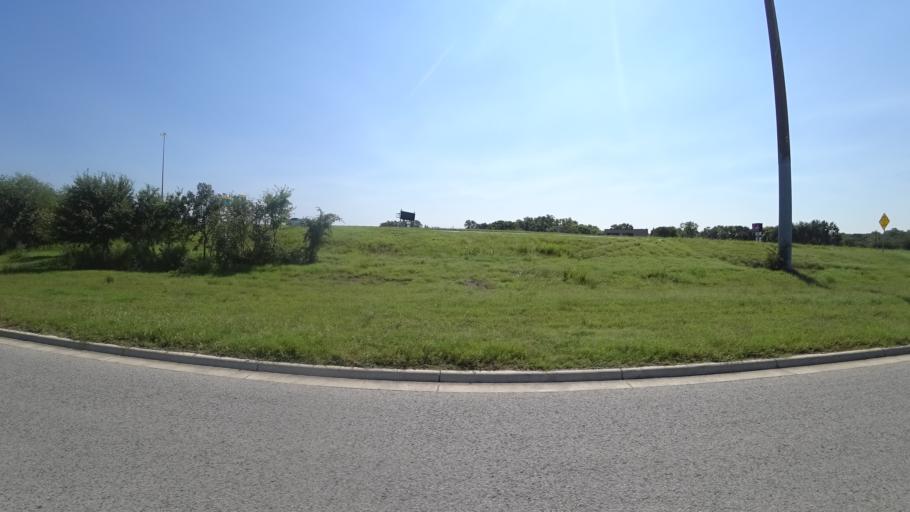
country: US
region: Texas
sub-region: Travis County
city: Austin
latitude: 30.3253
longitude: -97.6758
